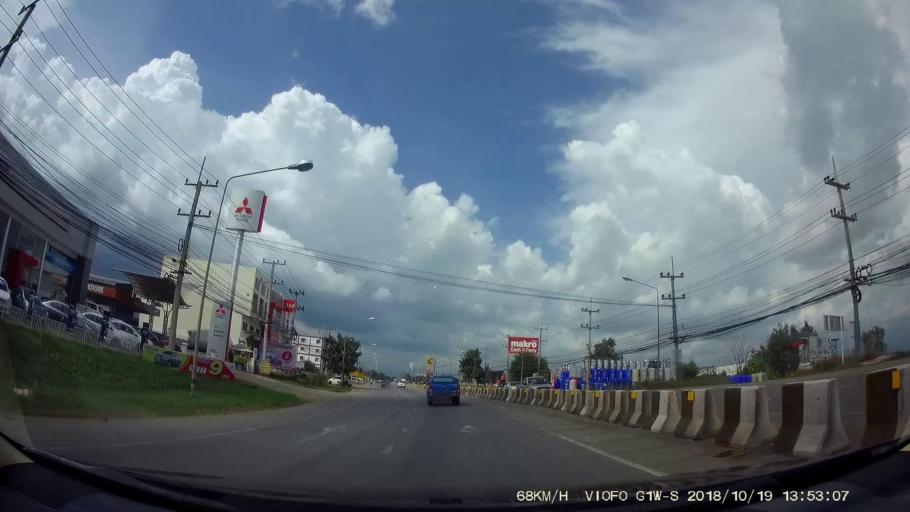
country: TH
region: Chaiyaphum
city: Chaiyaphum
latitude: 15.7740
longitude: 102.0259
